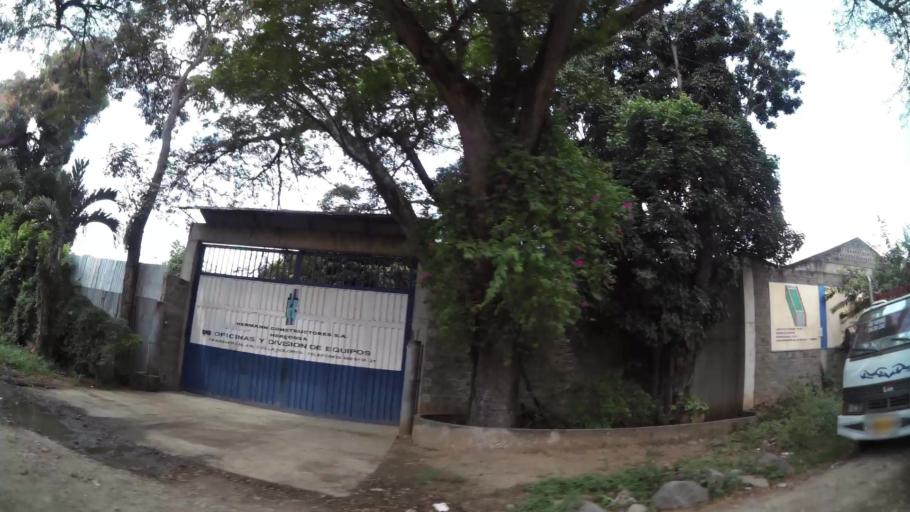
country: CO
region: Valle del Cauca
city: Cali
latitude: 3.4989
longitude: -76.4735
